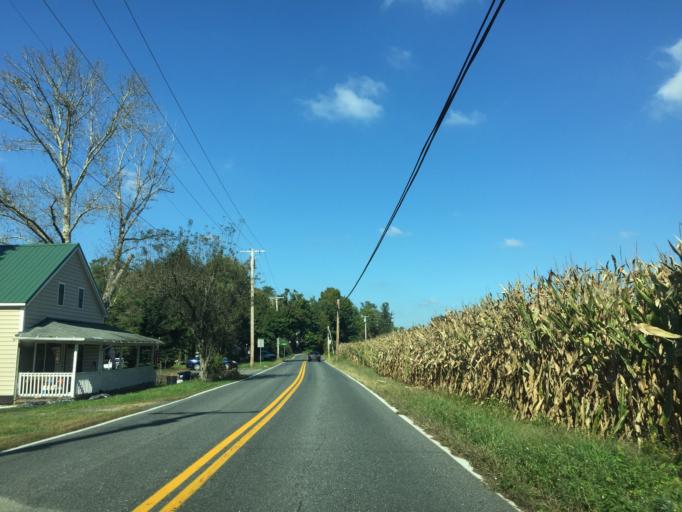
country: US
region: Maryland
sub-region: Harford County
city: Fallston
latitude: 39.5445
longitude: -76.4420
